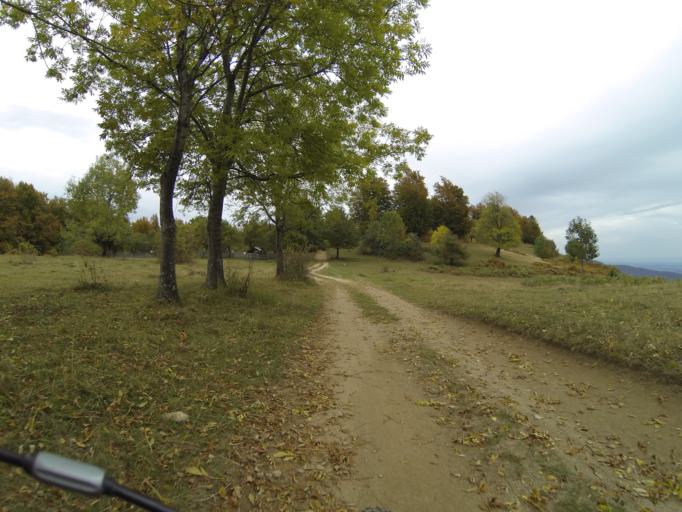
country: RO
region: Gorj
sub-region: Comuna Pades
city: Closani
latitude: 45.0949
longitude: 22.8379
